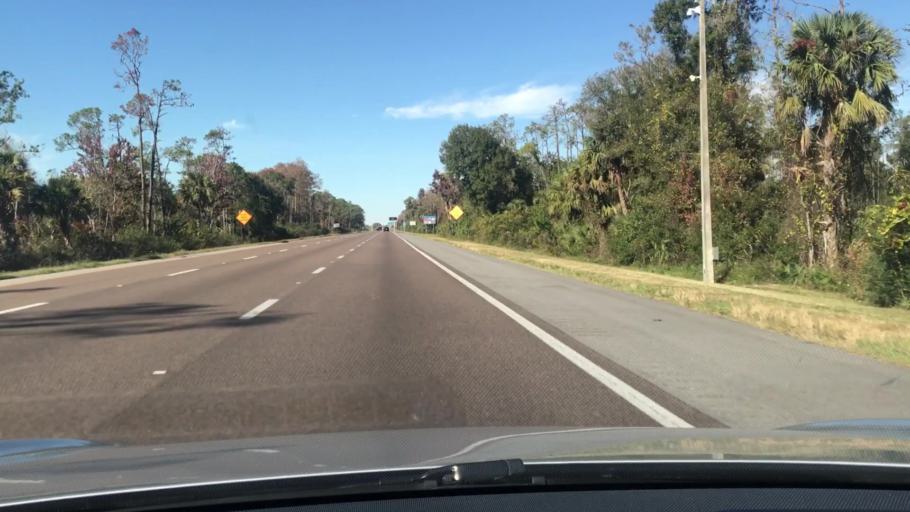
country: US
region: Florida
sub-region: Volusia County
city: Glencoe
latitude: 28.9999
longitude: -80.9791
